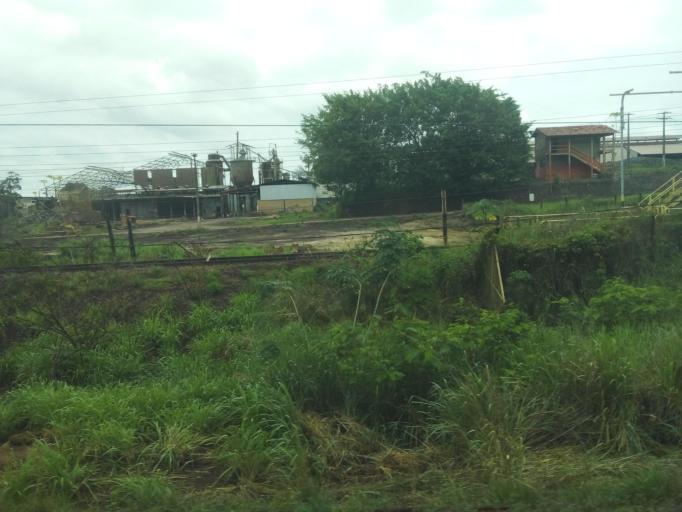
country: BR
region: Maranhao
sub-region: Santa Ines
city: Santa Ines
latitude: -3.6987
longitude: -45.4221
